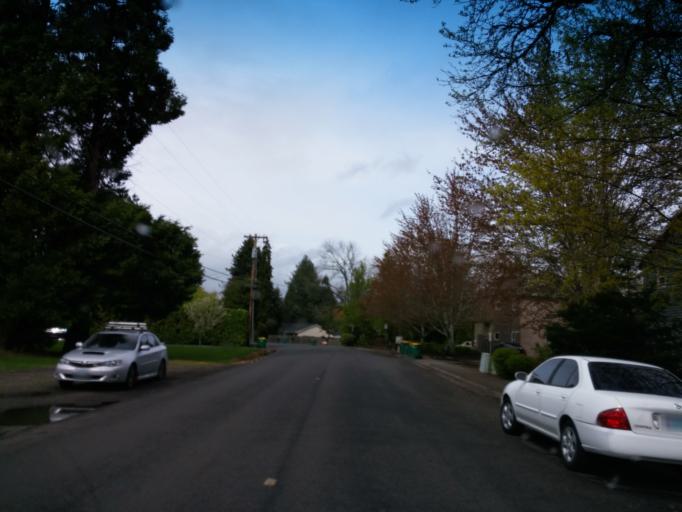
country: US
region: Oregon
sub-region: Washington County
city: Cedar Mill
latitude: 45.5159
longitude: -122.8316
